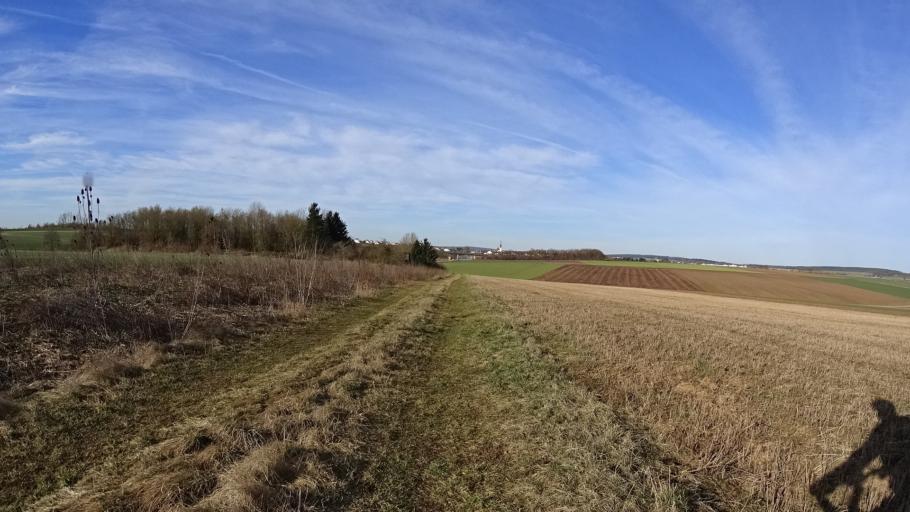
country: DE
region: Bavaria
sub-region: Upper Bavaria
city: Eitensheim
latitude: 48.8188
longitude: 11.3431
